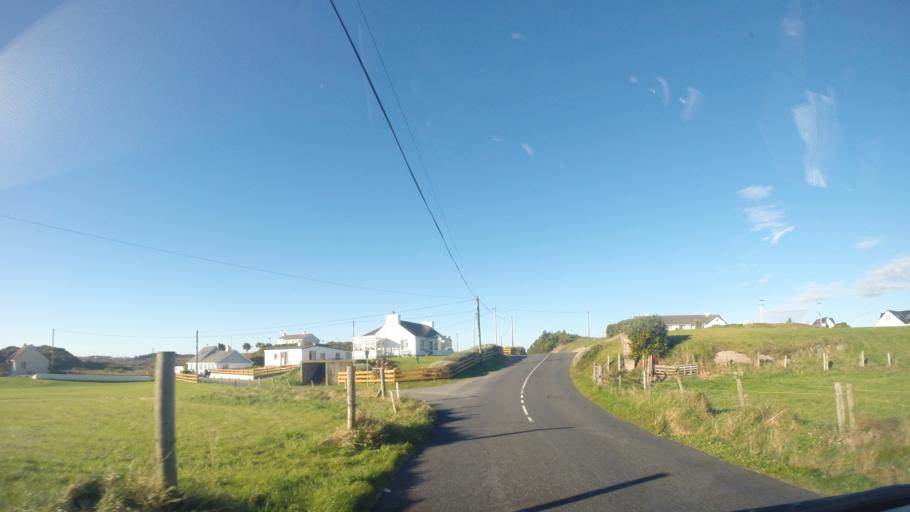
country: IE
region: Ulster
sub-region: County Donegal
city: Dungloe
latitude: 55.0317
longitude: -8.3665
